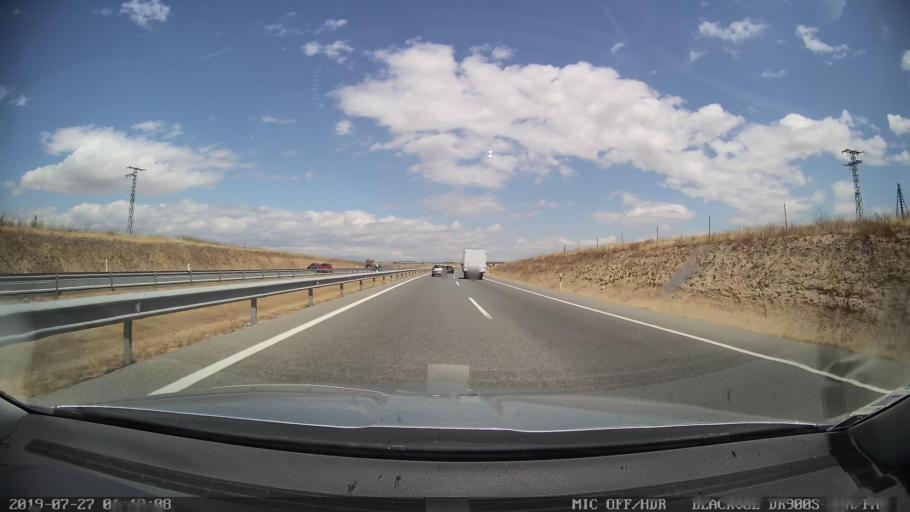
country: ES
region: Castille-La Mancha
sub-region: Province of Toledo
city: Quismondo
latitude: 40.1068
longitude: -4.3321
